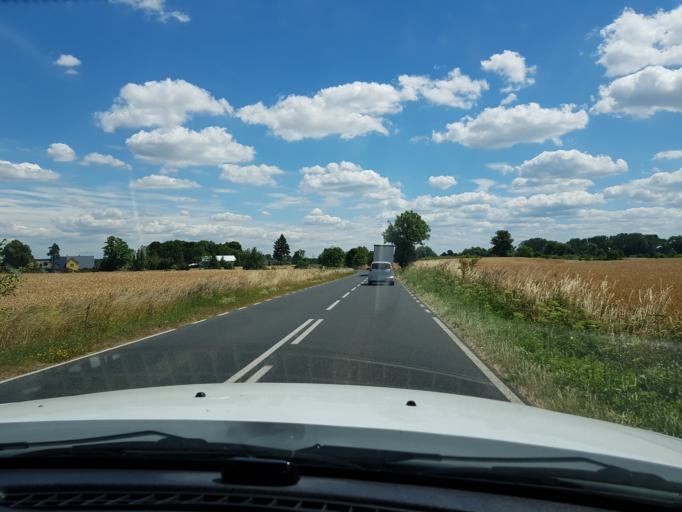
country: PL
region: West Pomeranian Voivodeship
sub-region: Powiat mysliborski
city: Mysliborz
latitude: 52.9065
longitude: 14.9416
